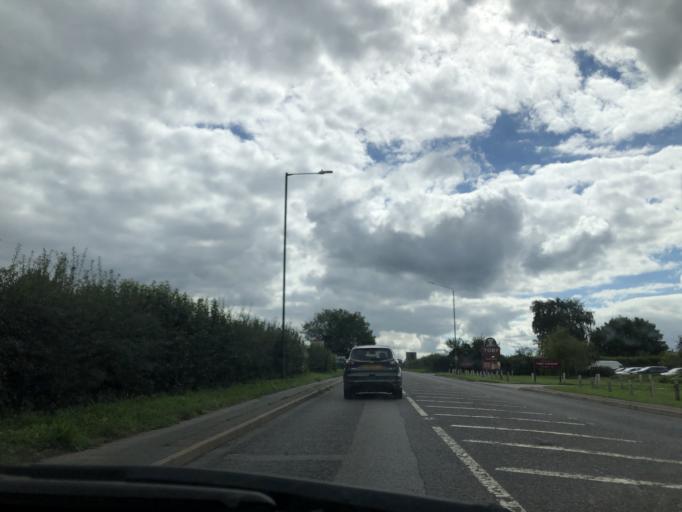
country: GB
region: England
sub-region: Kent
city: Halstead
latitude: 51.3320
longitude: 0.1486
